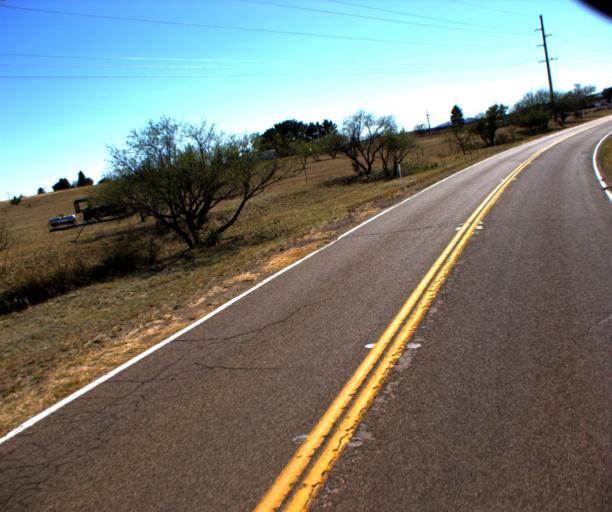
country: US
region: Arizona
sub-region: Pima County
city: Corona de Tucson
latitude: 31.6737
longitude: -110.6529
